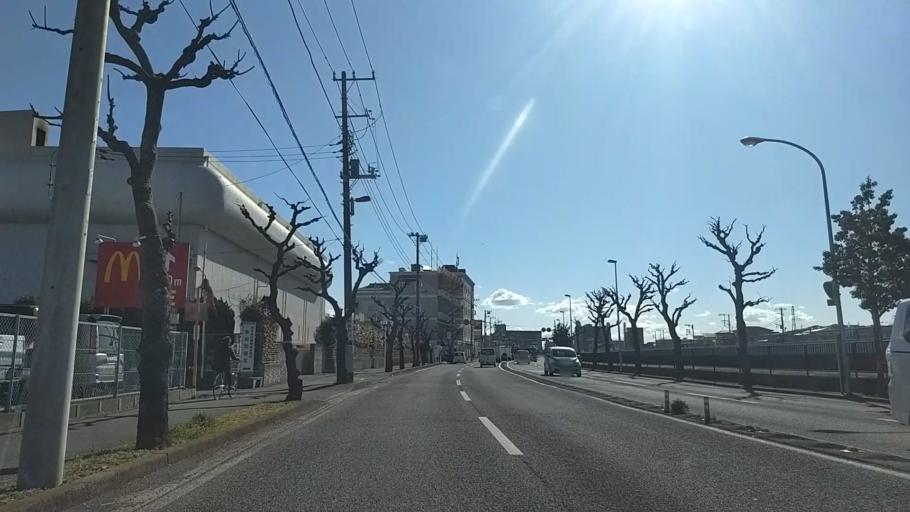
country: JP
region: Kanagawa
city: Yokosuka
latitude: 35.2400
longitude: 139.6957
